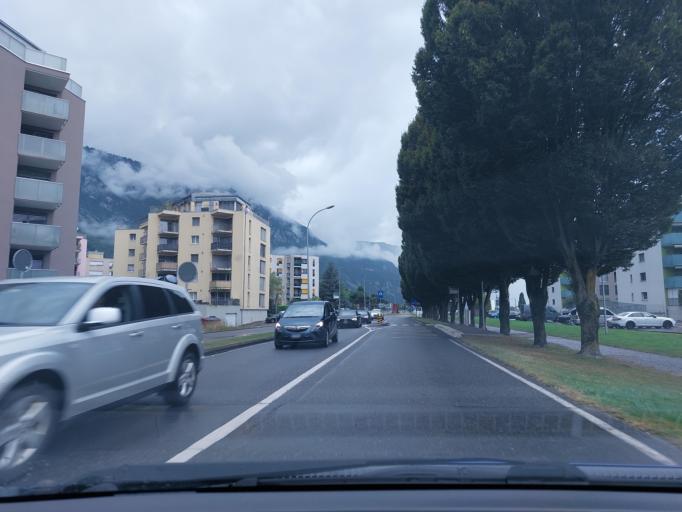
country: CH
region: Valais
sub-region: Monthey District
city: Collombey
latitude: 46.2750
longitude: 6.9412
